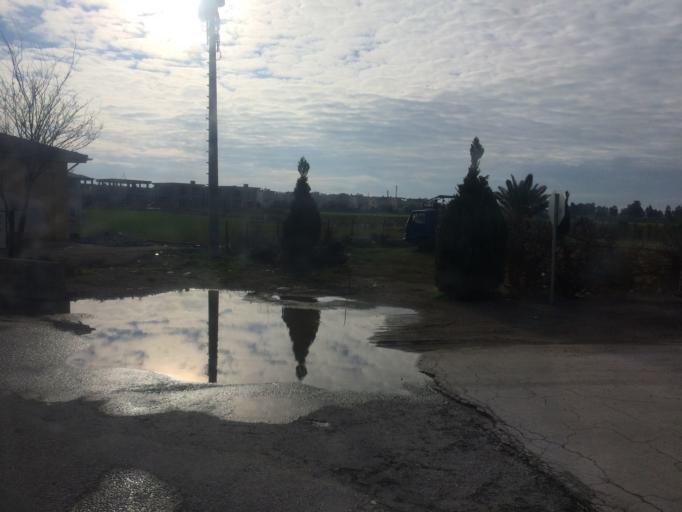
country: TR
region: Izmir
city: Menemen
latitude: 38.4997
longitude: 26.9599
